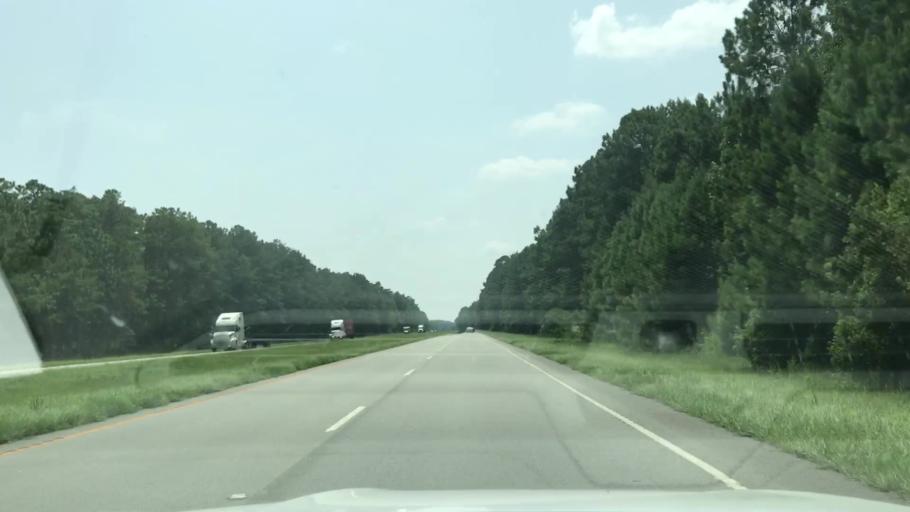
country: US
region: South Carolina
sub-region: Charleston County
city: Awendaw
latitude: 33.1380
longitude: -79.4418
